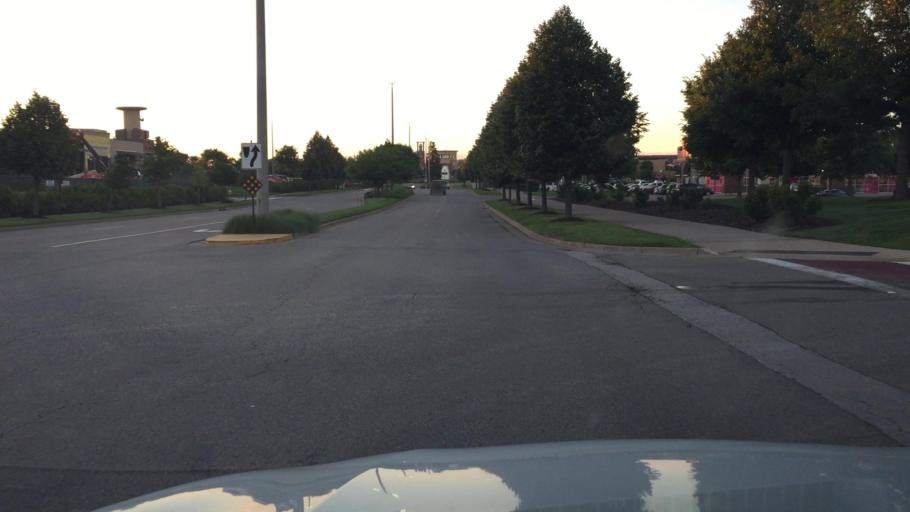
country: US
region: Iowa
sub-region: Polk County
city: Clive
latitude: 41.5634
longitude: -93.8037
